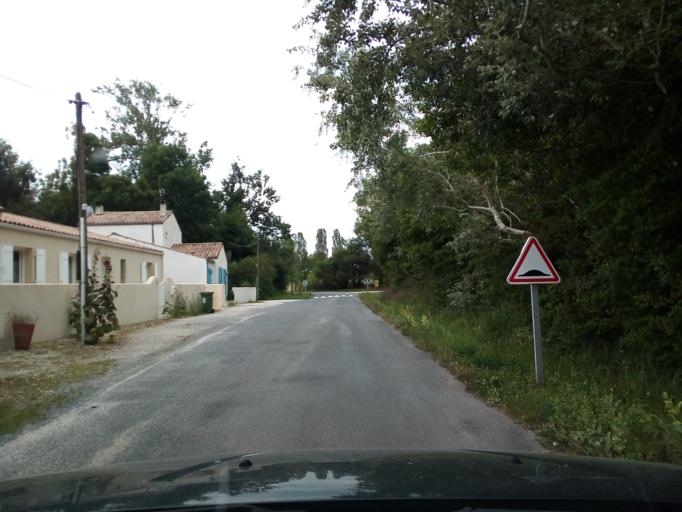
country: FR
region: Poitou-Charentes
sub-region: Departement de la Charente-Maritime
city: Dolus-d'Oleron
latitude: 45.9231
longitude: -1.2729
